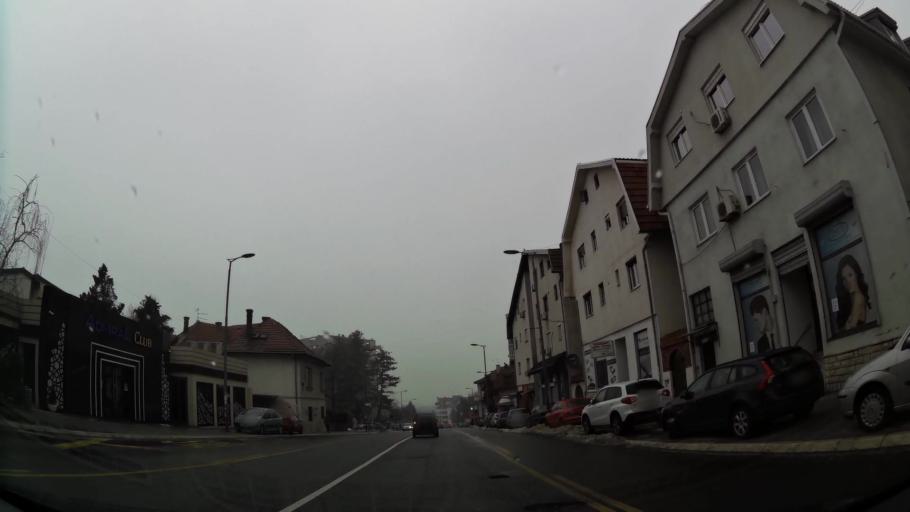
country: RS
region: Central Serbia
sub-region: Belgrade
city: Cukarica
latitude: 44.7837
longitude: 20.4180
